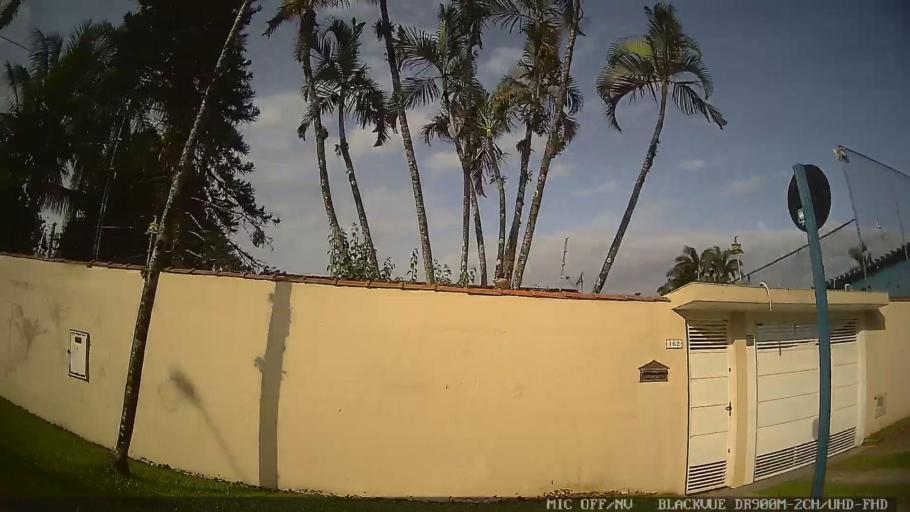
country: BR
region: Sao Paulo
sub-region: Bertioga
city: Bertioga
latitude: -23.8158
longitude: -46.0469
